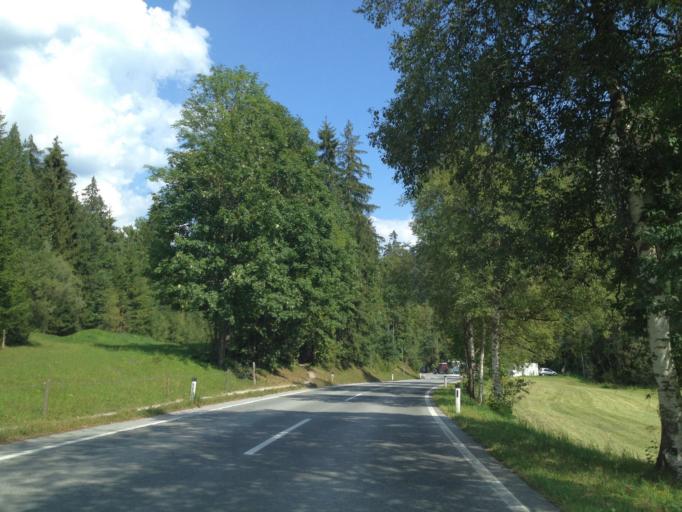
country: AT
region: Styria
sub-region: Politischer Bezirk Liezen
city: Schladming
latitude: 47.4241
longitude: 13.6976
